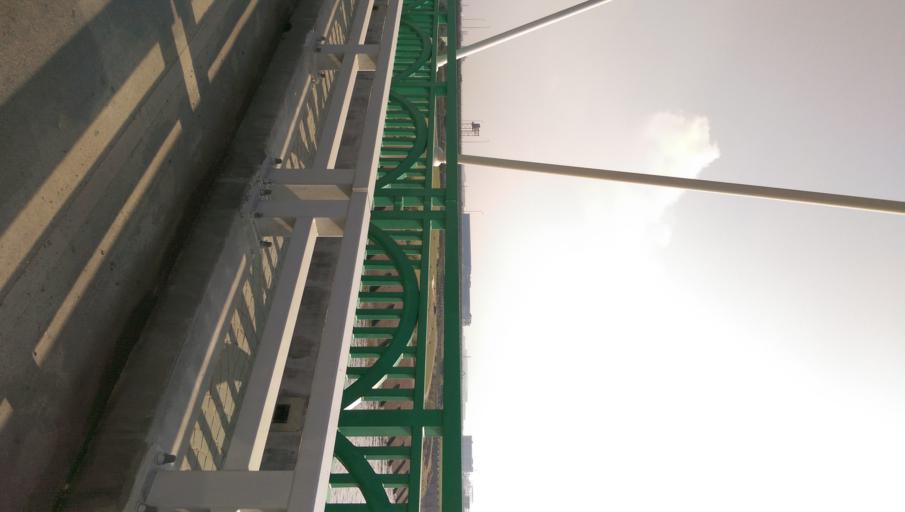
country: TW
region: Taiwan
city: Taoyuan City
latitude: 25.1182
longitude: 121.2484
